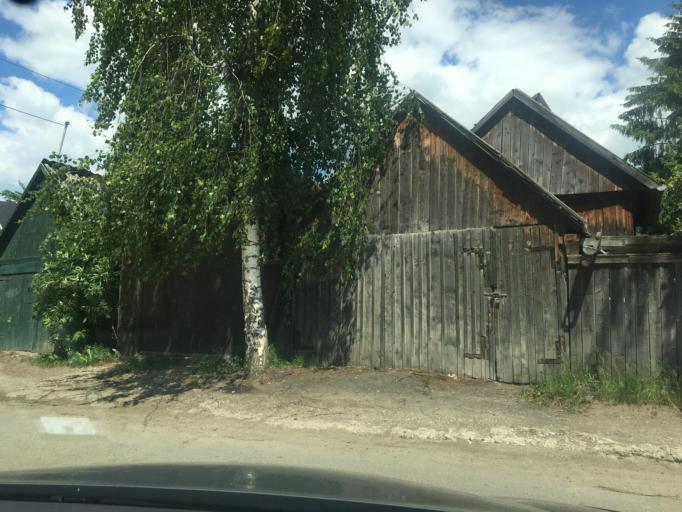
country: RO
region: Harghita
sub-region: Municipiul Gheorgheni
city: Gheorgheni
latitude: 46.7190
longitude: 25.5899
